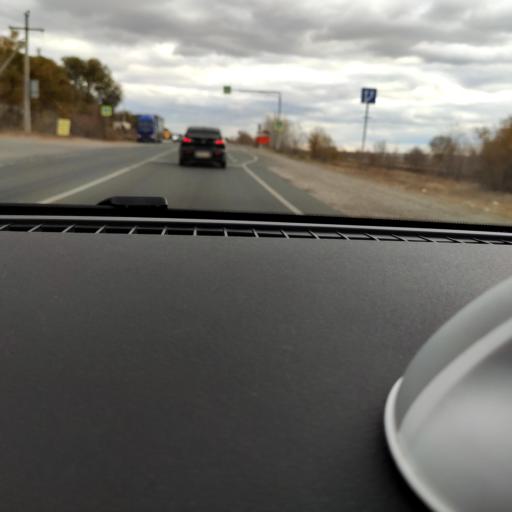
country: RU
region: Samara
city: Samara
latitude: 53.1261
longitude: 50.1734
